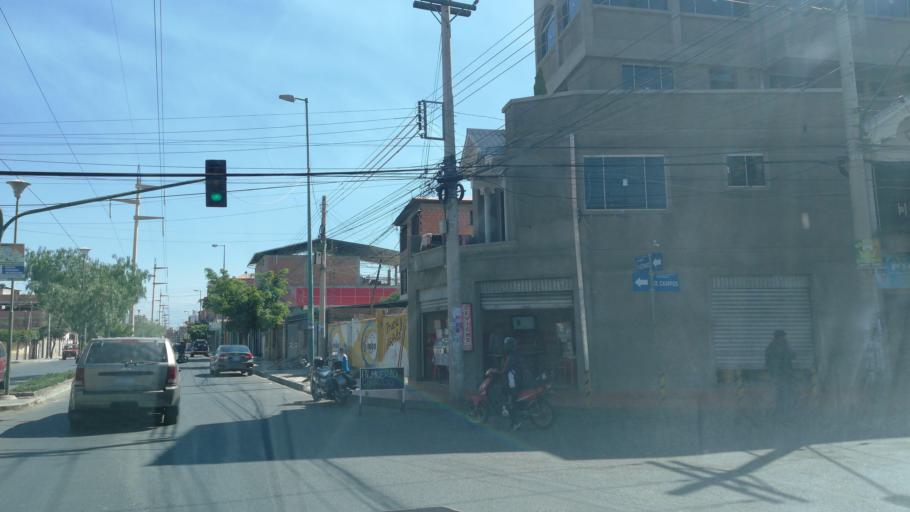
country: BO
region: Cochabamba
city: Cochabamba
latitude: -17.3893
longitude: -66.2147
